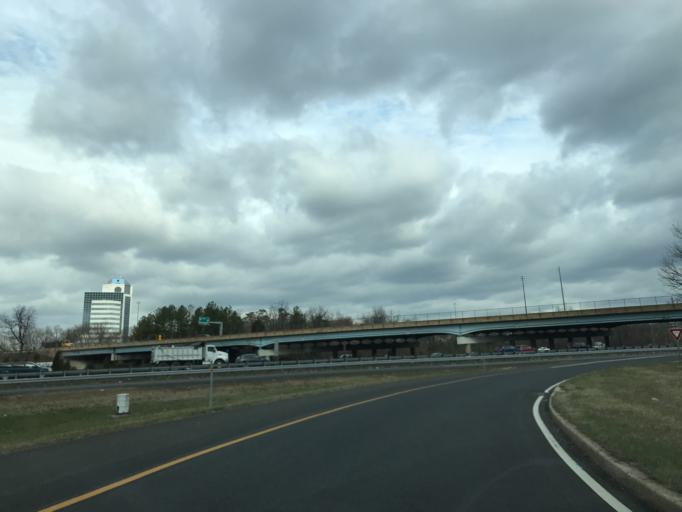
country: US
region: Maryland
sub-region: Prince George's County
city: Calverton
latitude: 39.0498
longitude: -76.9295
